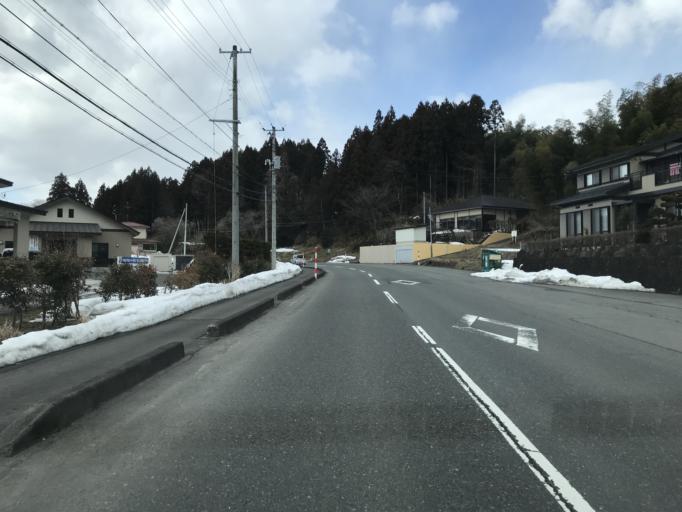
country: JP
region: Miyagi
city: Furukawa
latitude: 38.7369
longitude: 140.7694
